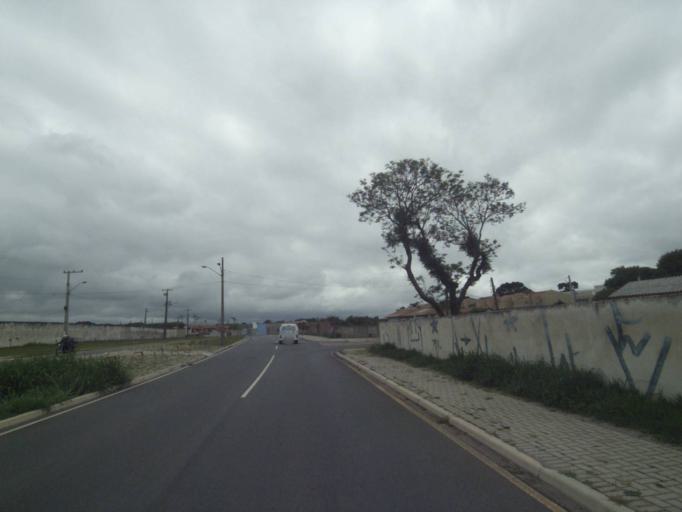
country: BR
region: Parana
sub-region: Pinhais
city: Pinhais
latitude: -25.4331
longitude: -49.2185
